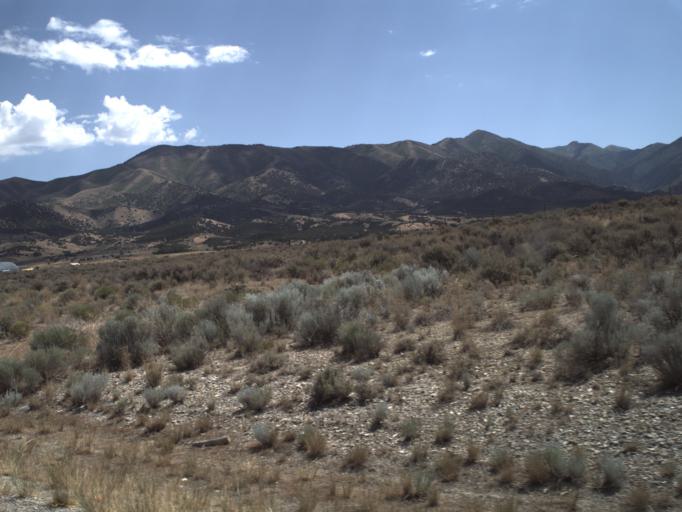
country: US
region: Utah
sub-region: Tooele County
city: Tooele
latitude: 40.4326
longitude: -112.3769
